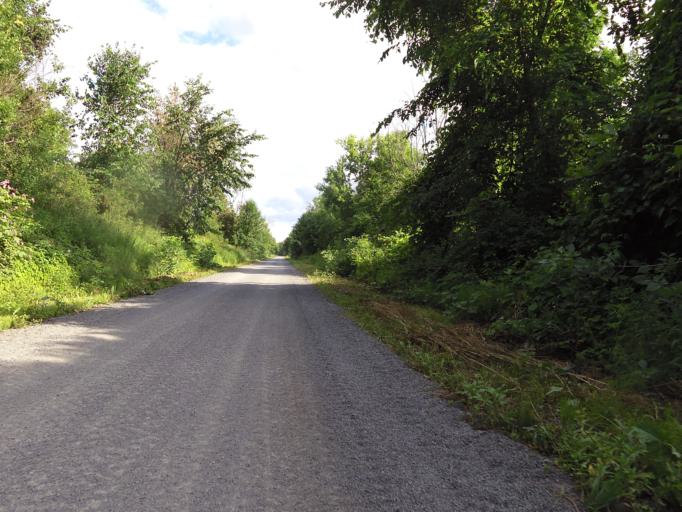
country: CA
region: Ontario
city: Arnprior
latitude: 45.3214
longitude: -76.2866
